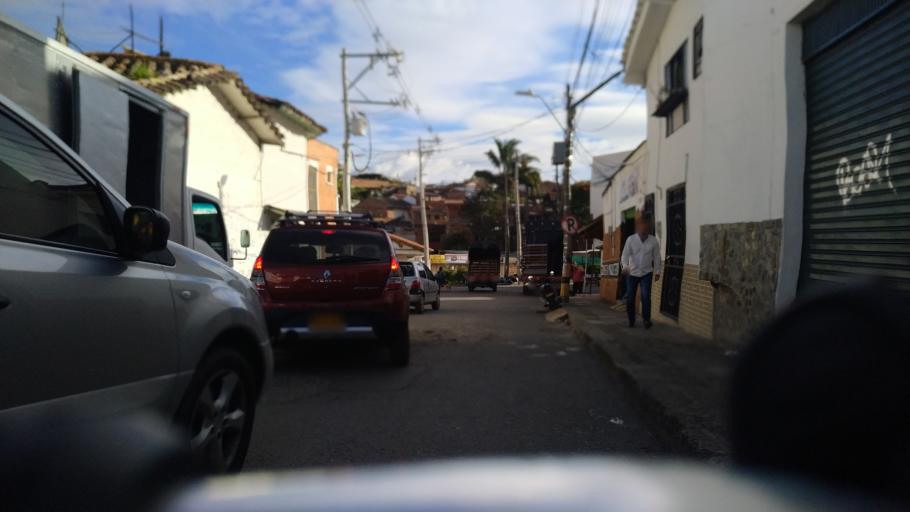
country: CO
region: Antioquia
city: Rionegro
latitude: 6.1538
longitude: -75.3752
